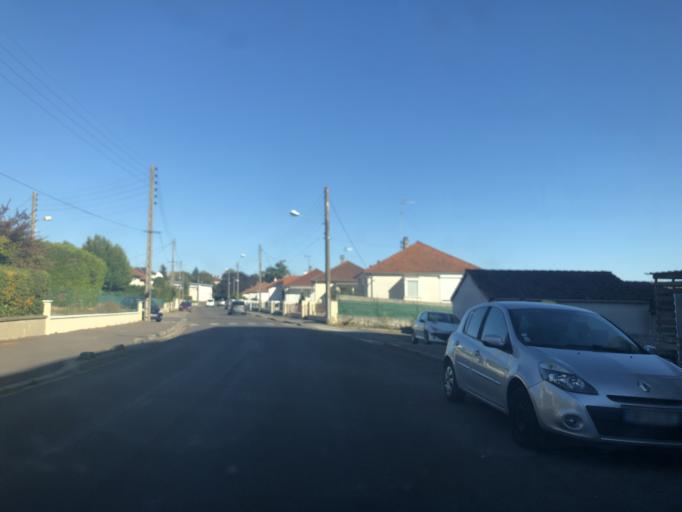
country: FR
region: Bourgogne
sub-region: Departement de l'Yonne
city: Joigny
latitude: 47.9806
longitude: 3.4161
